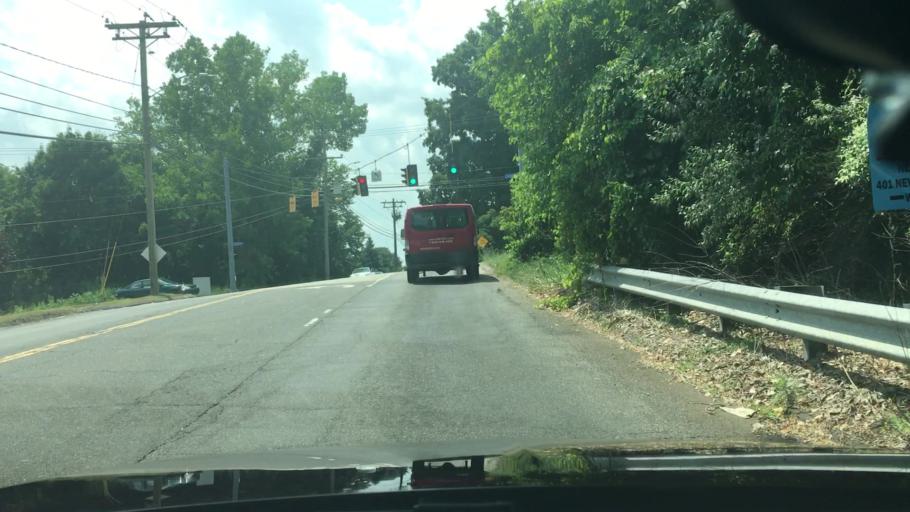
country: US
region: Connecticut
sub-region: Hartford County
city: Kensington
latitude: 41.6547
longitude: -72.7394
